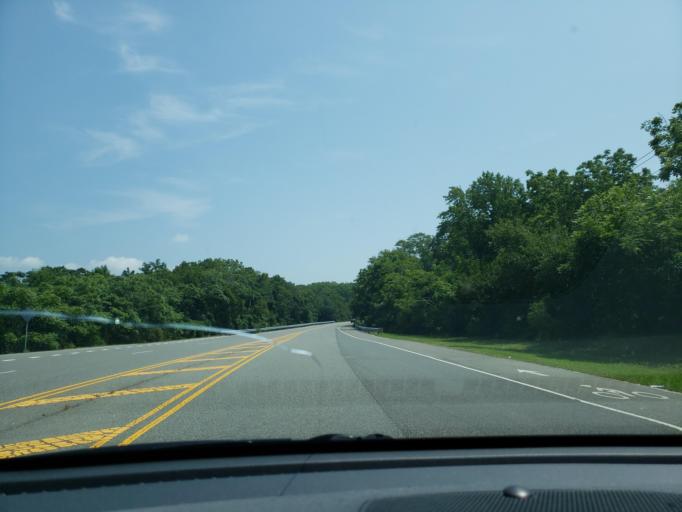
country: US
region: New Jersey
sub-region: Cape May County
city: North Cape May
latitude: 38.9738
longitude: -74.9351
